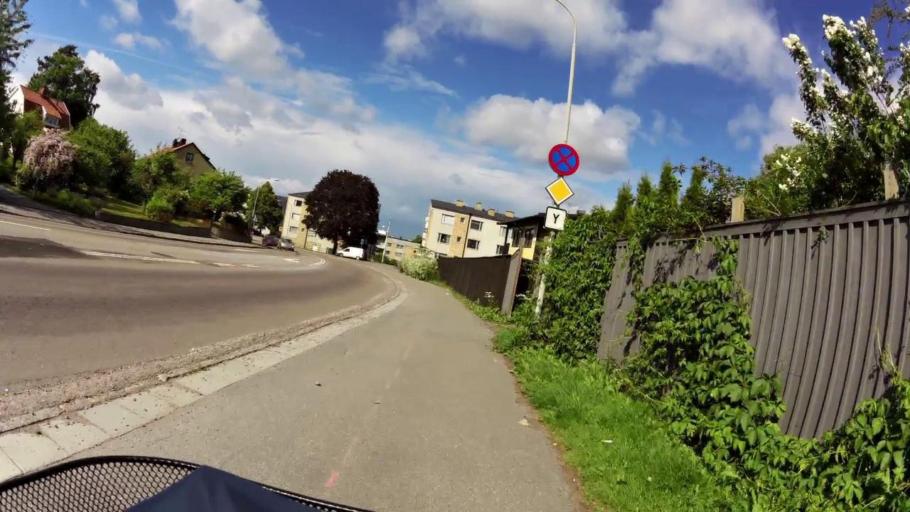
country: SE
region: OEstergoetland
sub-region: Linkopings Kommun
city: Linkoping
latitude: 58.3956
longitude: 15.6518
